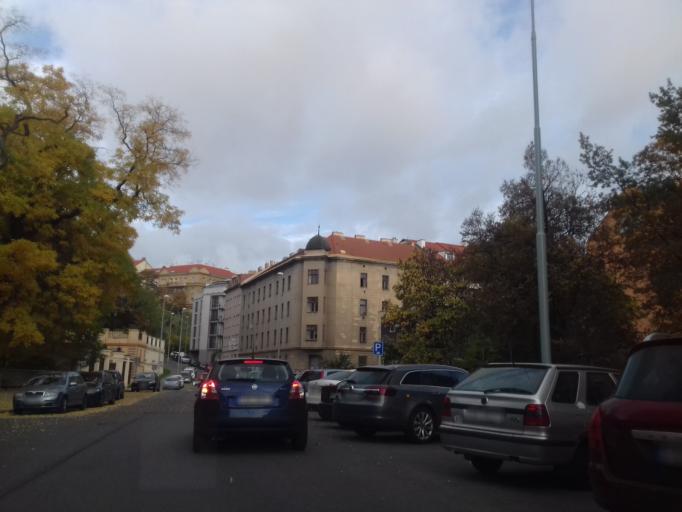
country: CZ
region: Praha
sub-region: Praha 8
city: Karlin
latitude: 50.0676
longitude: 14.4487
